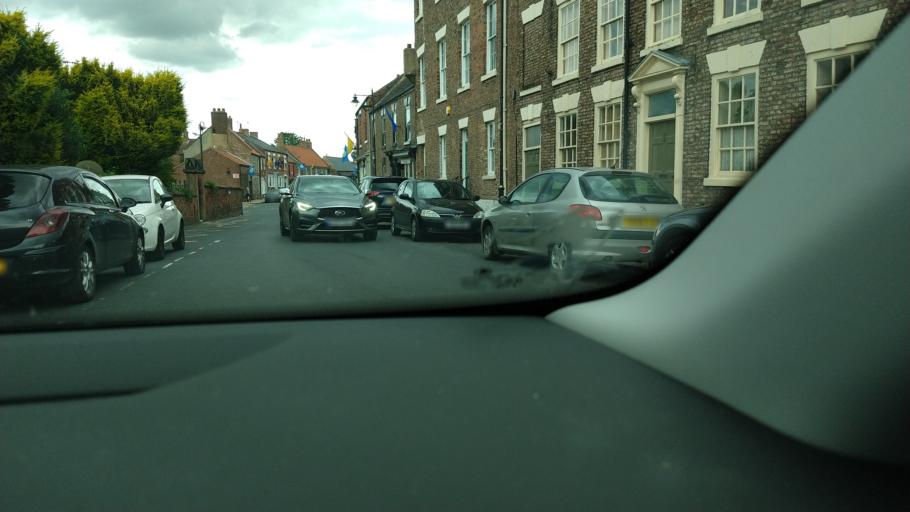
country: GB
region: England
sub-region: East Riding of Yorkshire
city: Snaith
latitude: 53.6917
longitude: -1.0310
